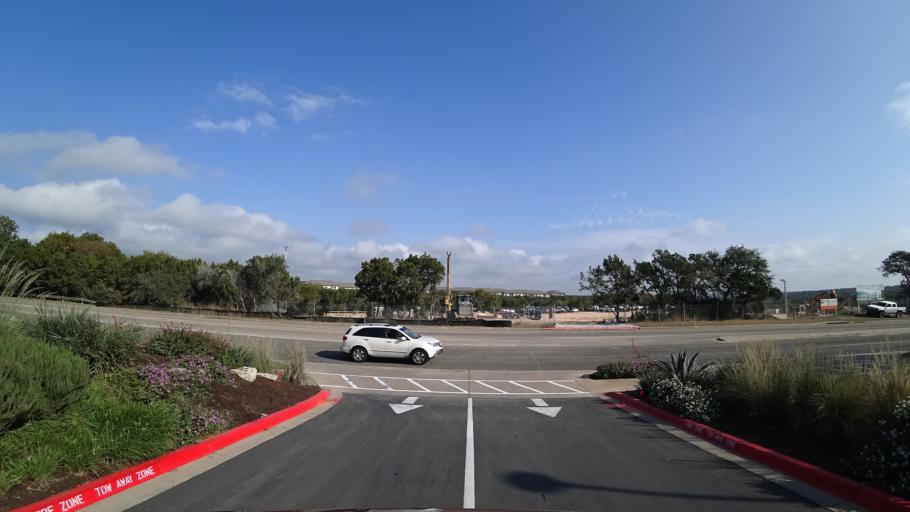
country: US
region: Texas
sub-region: Williamson County
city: Anderson Mill
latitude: 30.4049
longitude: -97.8491
